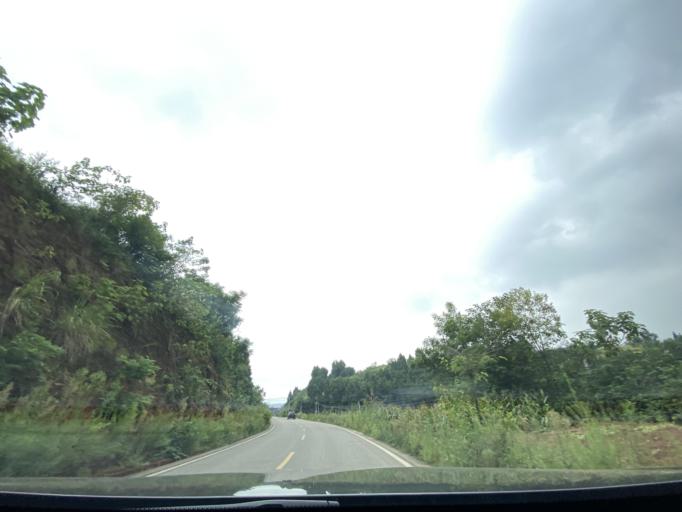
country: CN
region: Sichuan
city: Jiancheng
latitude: 30.5390
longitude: 104.5240
